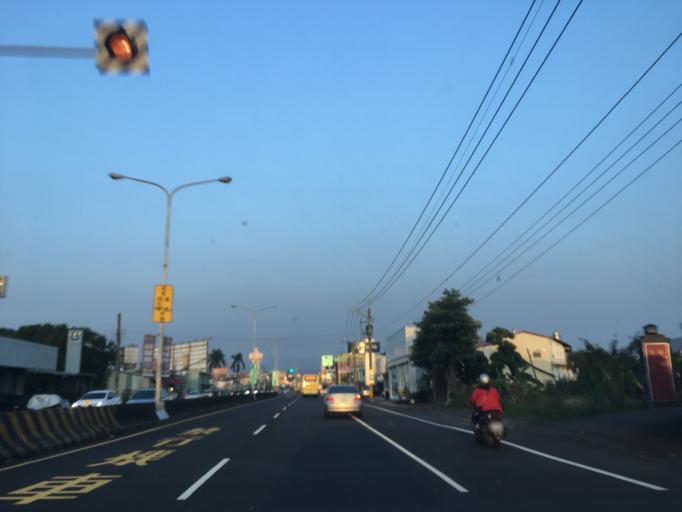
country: TW
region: Taiwan
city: Zhongxing New Village
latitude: 23.9873
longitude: 120.6768
